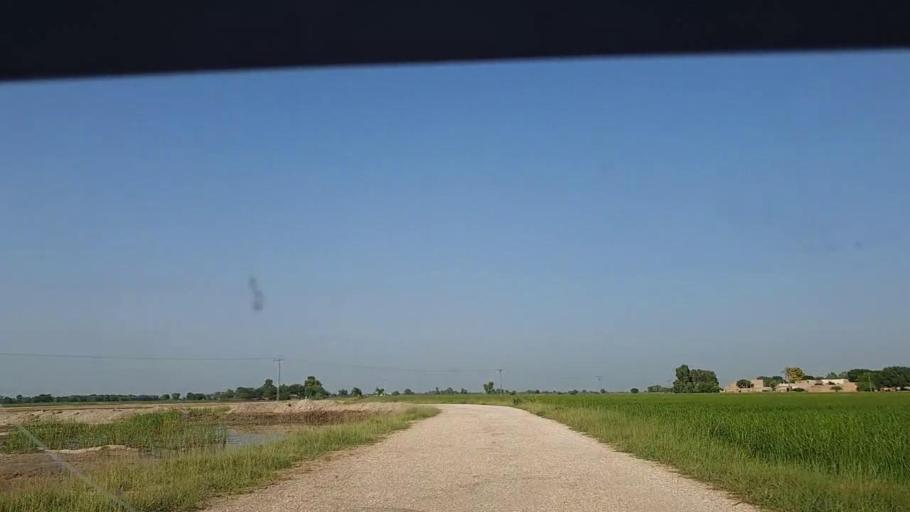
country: PK
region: Sindh
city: Tangwani
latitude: 28.2634
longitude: 69.0104
